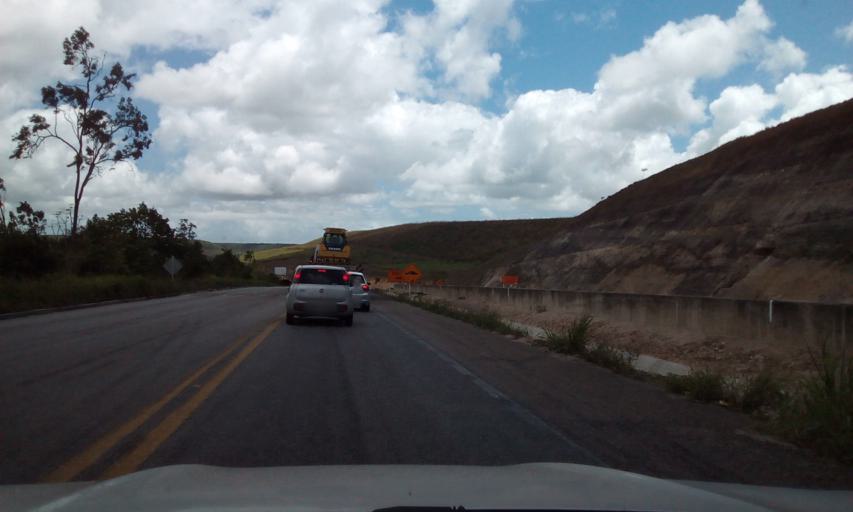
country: BR
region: Alagoas
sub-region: Sao Miguel Dos Campos
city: Sao Miguel dos Campos
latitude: -9.8928
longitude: -36.1498
